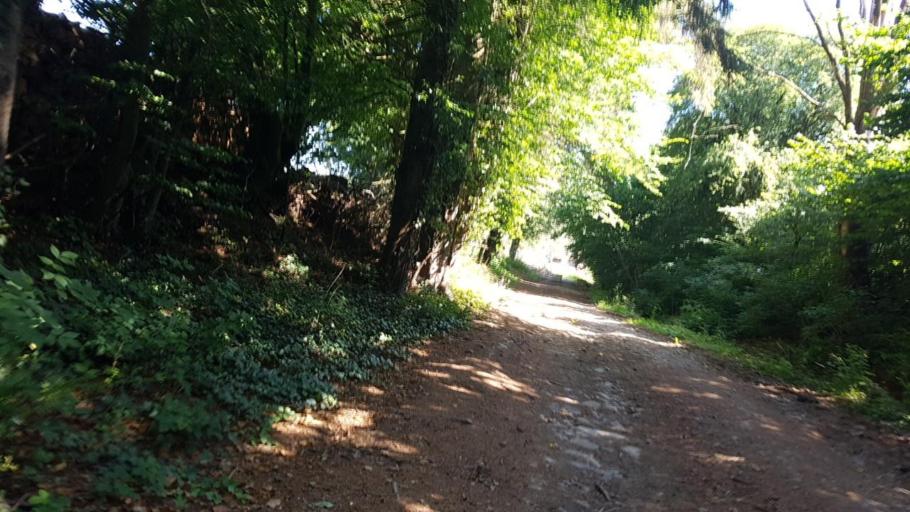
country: FR
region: Nord-Pas-de-Calais
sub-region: Departement du Nord
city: Anor
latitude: 49.9717
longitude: 4.1195
